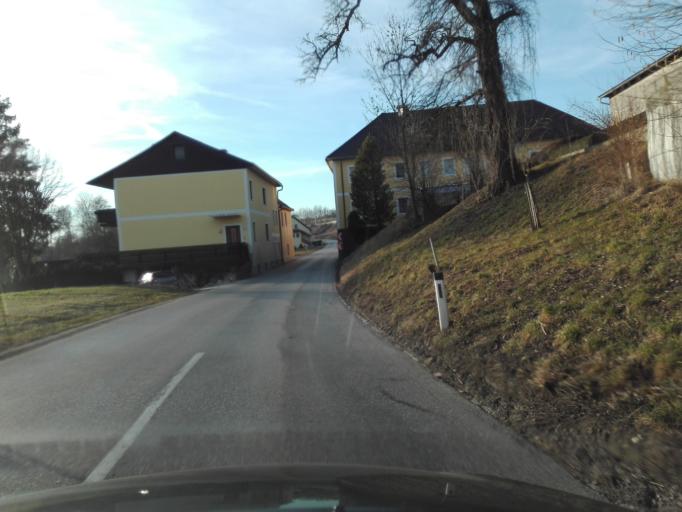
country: AT
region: Lower Austria
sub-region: Politischer Bezirk Amstetten
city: Haag
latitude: 48.1153
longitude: 14.5524
